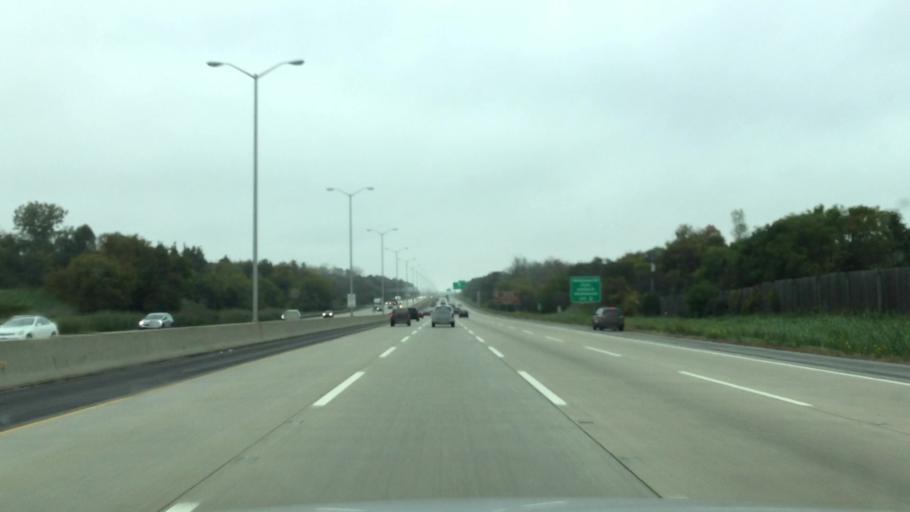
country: US
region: Illinois
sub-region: Lake County
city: Wadsworth
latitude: 42.4422
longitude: -87.9568
